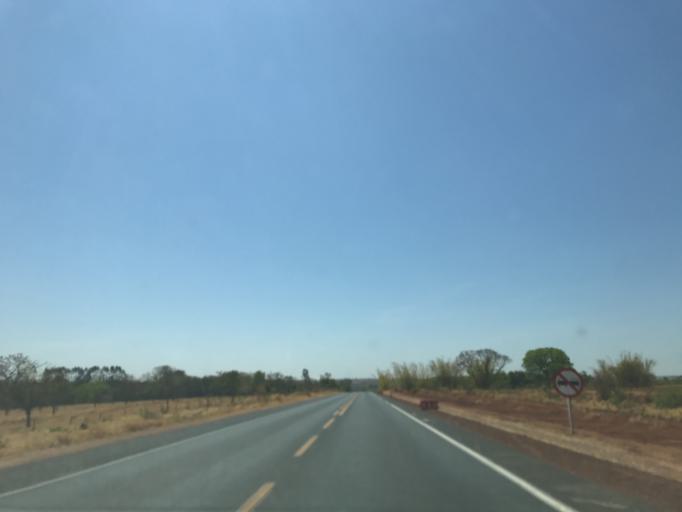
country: BR
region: Minas Gerais
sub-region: Prata
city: Prata
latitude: -19.3771
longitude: -48.8985
